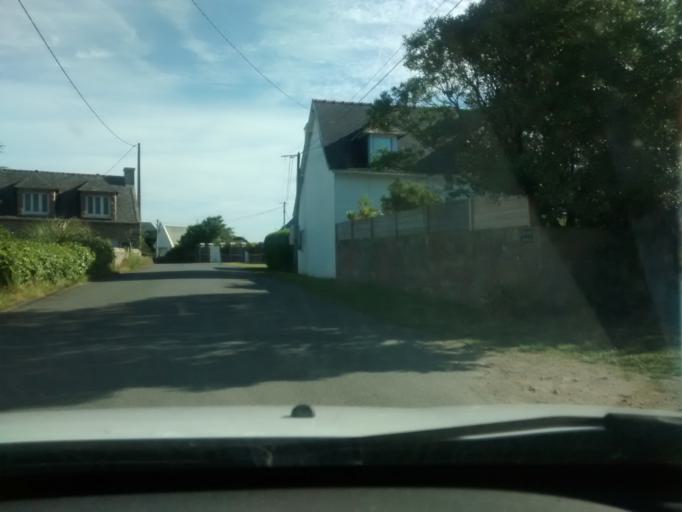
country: FR
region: Brittany
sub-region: Departement des Cotes-d'Armor
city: Plougrescant
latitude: 48.8600
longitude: -3.2190
